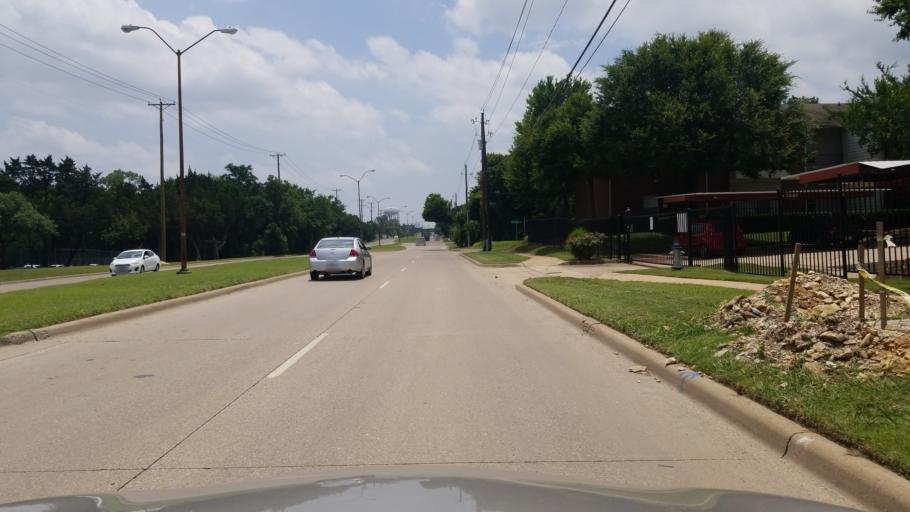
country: US
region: Texas
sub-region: Dallas County
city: Duncanville
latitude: 32.6861
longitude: -96.9087
